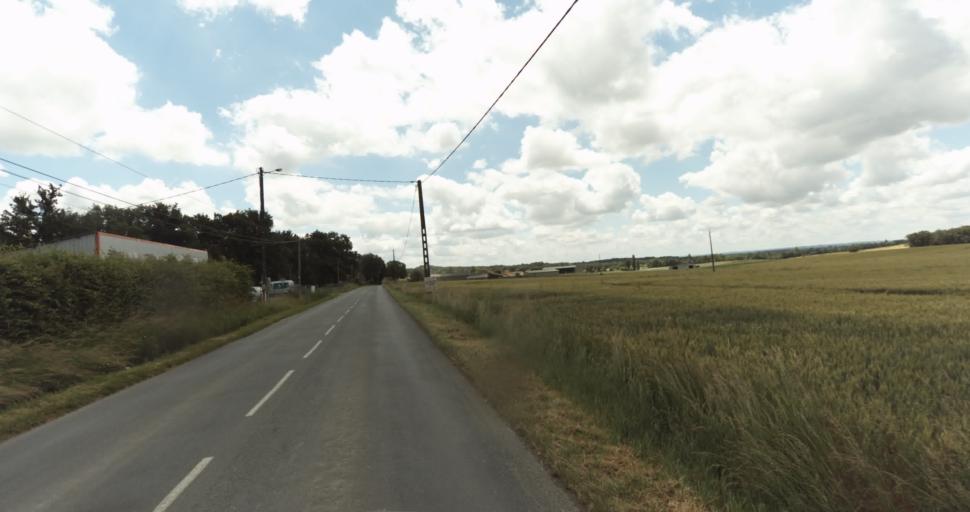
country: FR
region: Aquitaine
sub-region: Departement de la Dordogne
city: Beaumont-du-Perigord
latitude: 44.7301
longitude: 0.7562
